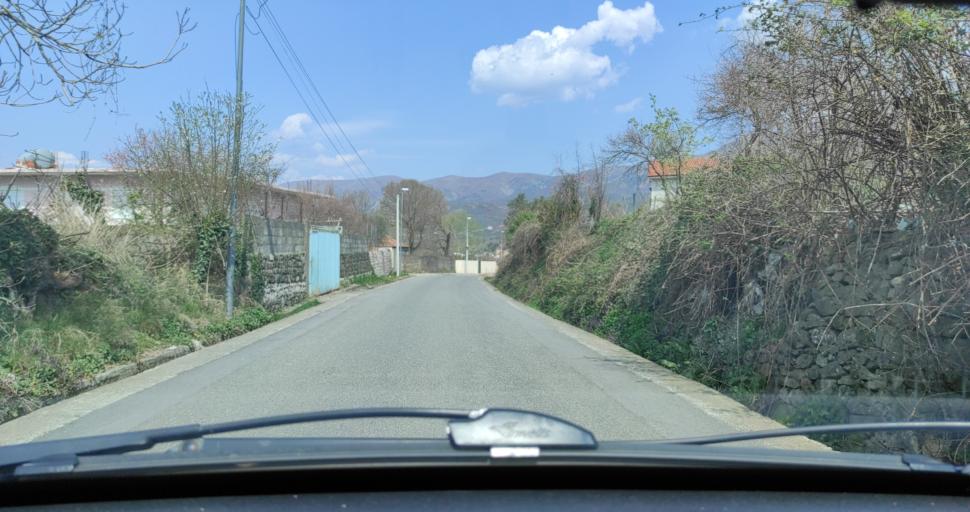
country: AL
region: Lezhe
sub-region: Rrethi i Lezhes
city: Kallmeti i Madh
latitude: 41.8557
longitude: 19.6952
